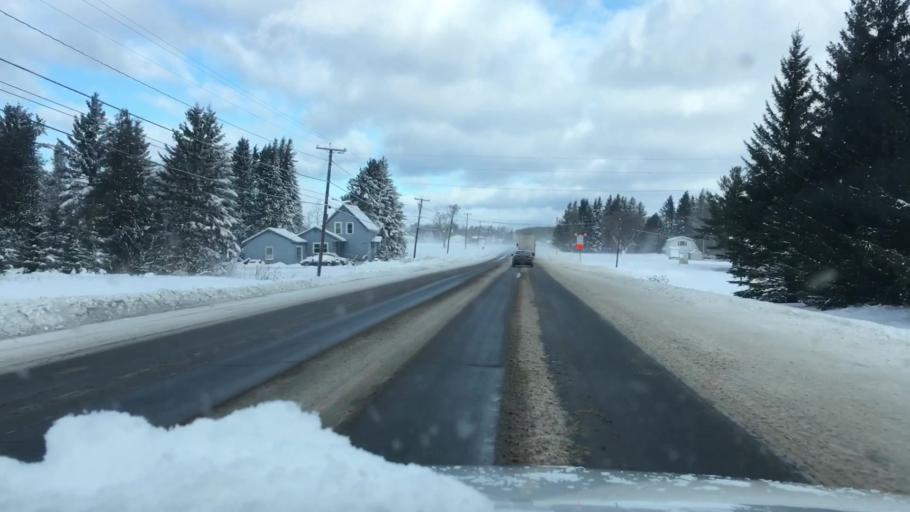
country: US
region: Maine
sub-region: Aroostook County
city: Caribou
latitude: 46.8059
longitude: -67.9937
